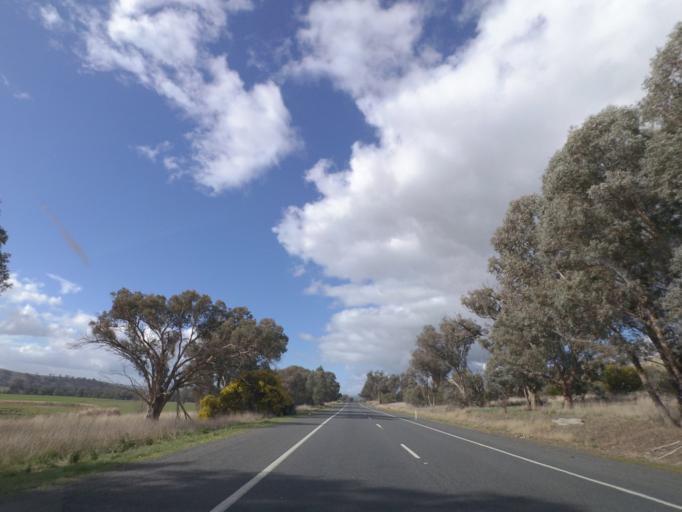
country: AU
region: New South Wales
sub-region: Greater Hume Shire
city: Holbrook
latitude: -35.6727
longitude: 147.3979
